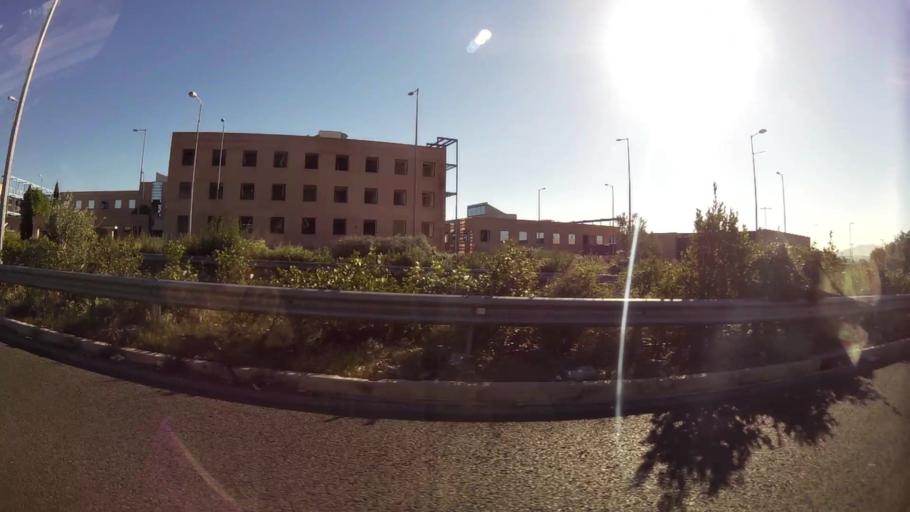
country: GR
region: Attica
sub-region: Nomarchia Anatolikis Attikis
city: Thrakomakedones
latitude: 38.1032
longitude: 23.7640
